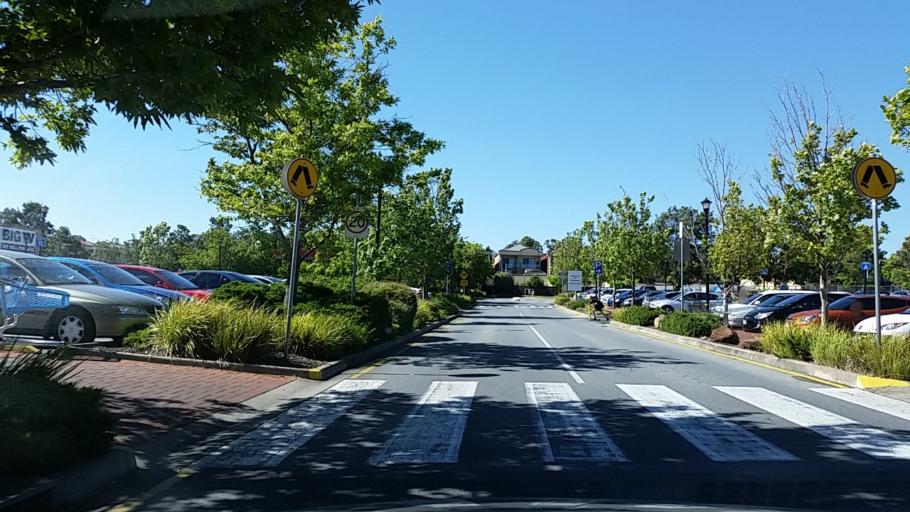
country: AU
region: South Australia
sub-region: Tea Tree Gully
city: Golden Grove
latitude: -34.7902
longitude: 138.6956
